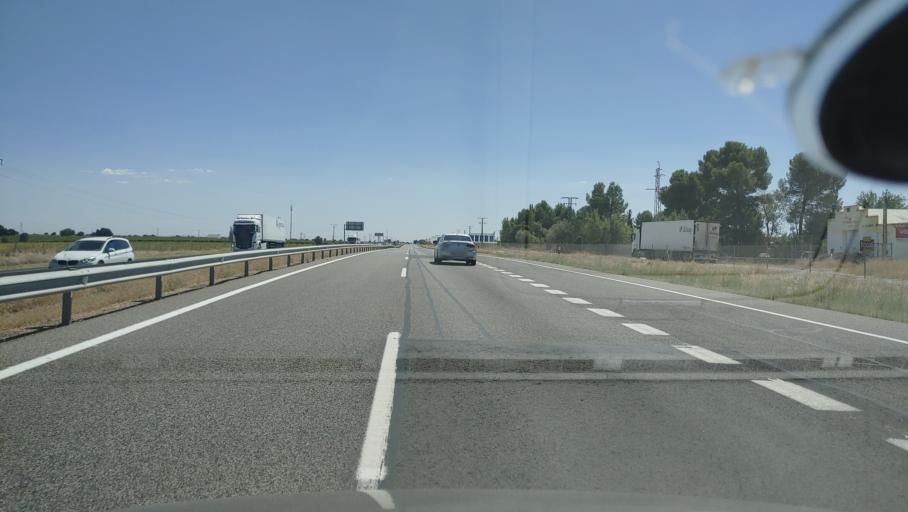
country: ES
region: Castille-La Mancha
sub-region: Provincia de Ciudad Real
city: Villarta de San Juan
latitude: 39.2160
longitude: -3.4126
